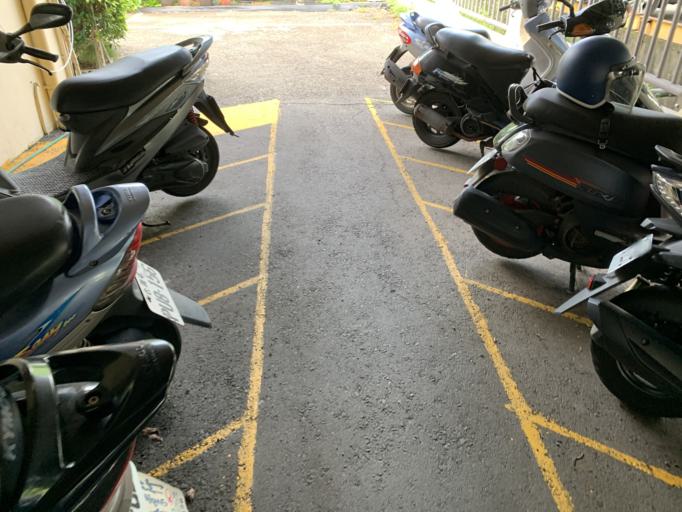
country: TW
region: Taiwan
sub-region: Taichung City
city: Taichung
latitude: 24.1742
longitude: 120.5993
